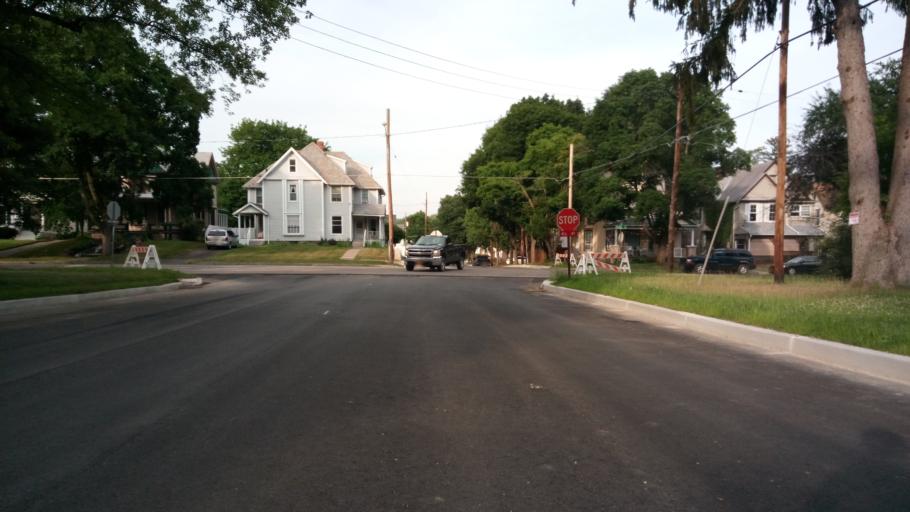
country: US
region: New York
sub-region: Chemung County
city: Elmira
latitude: 42.0877
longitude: -76.8225
